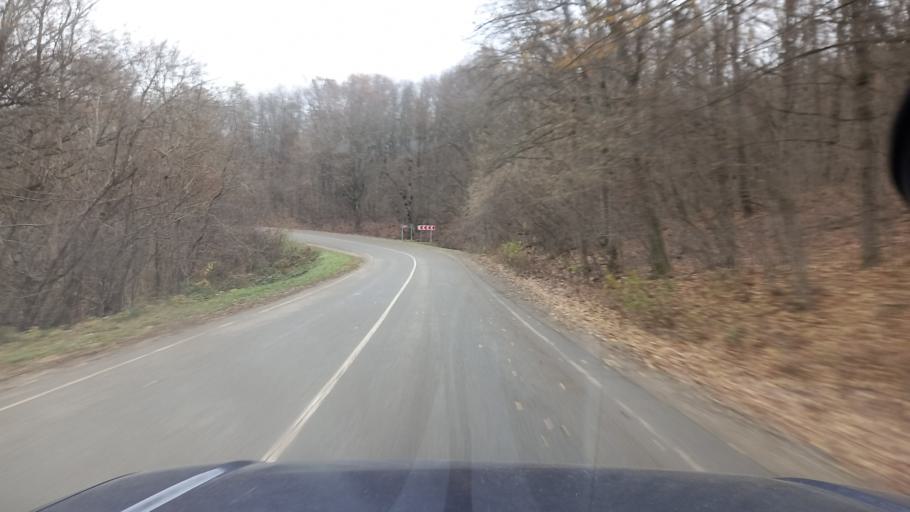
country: RU
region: Krasnodarskiy
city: Goryachiy Klyuch
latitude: 44.5425
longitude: 39.2562
